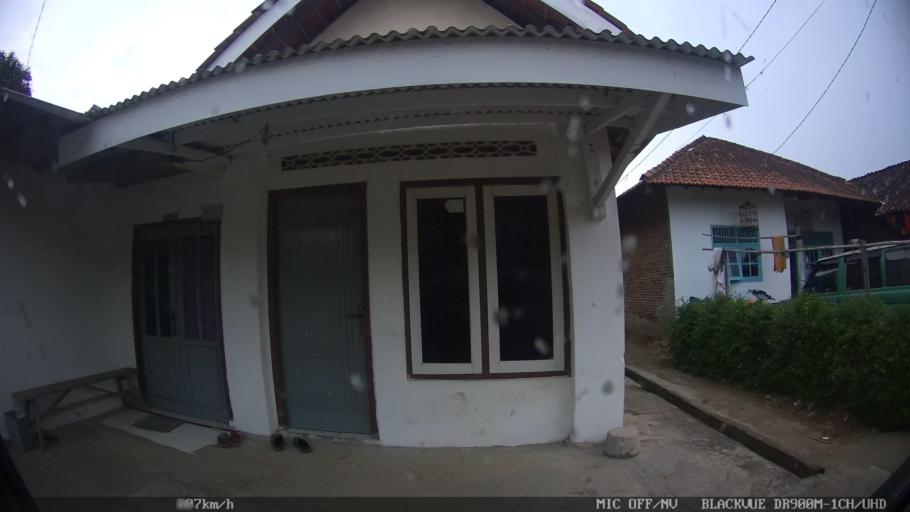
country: ID
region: Lampung
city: Kedaton
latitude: -5.3967
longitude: 105.2786
